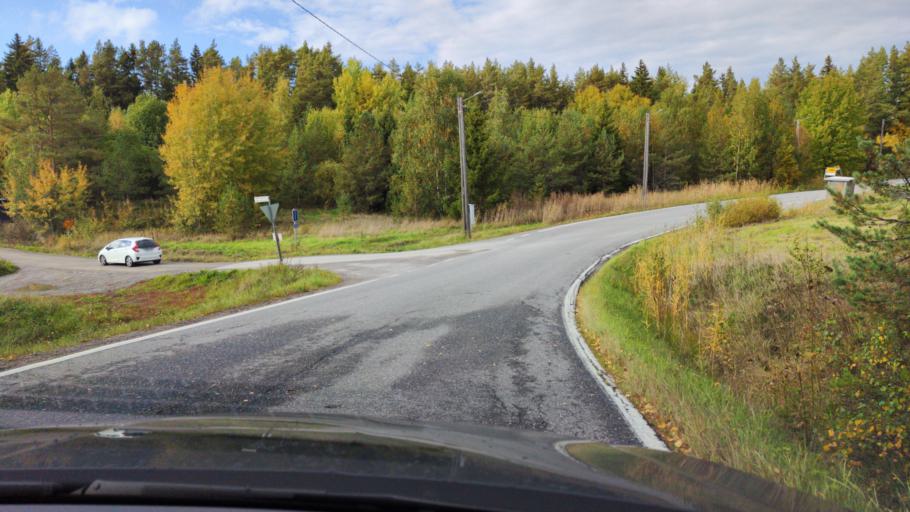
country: FI
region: Varsinais-Suomi
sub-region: Aboland-Turunmaa
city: Pargas
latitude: 60.3460
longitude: 22.1854
